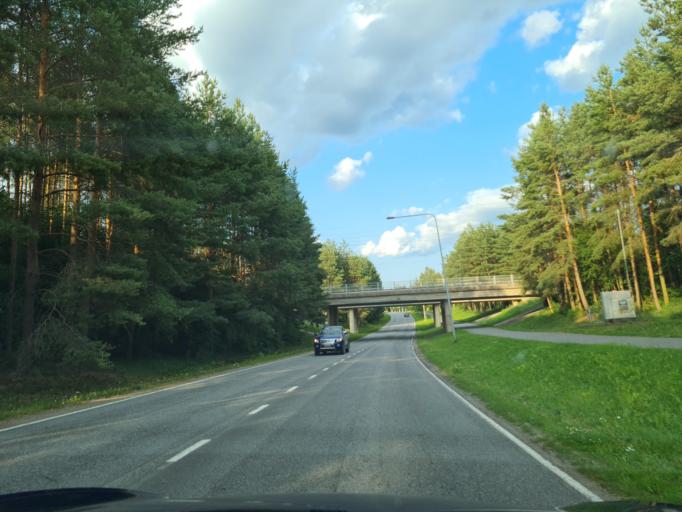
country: FI
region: Southern Ostrobothnia
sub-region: Seinaejoki
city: Lapua
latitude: 62.9743
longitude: 23.0116
